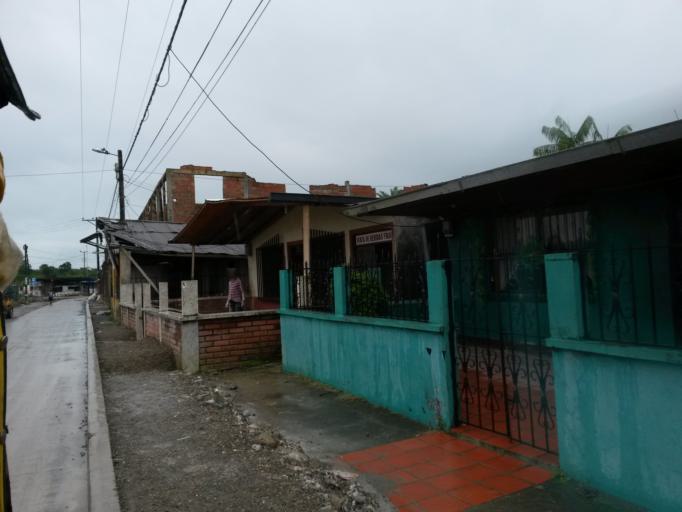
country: CO
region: Cauca
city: Guapi
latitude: 2.5738
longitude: -77.8938
